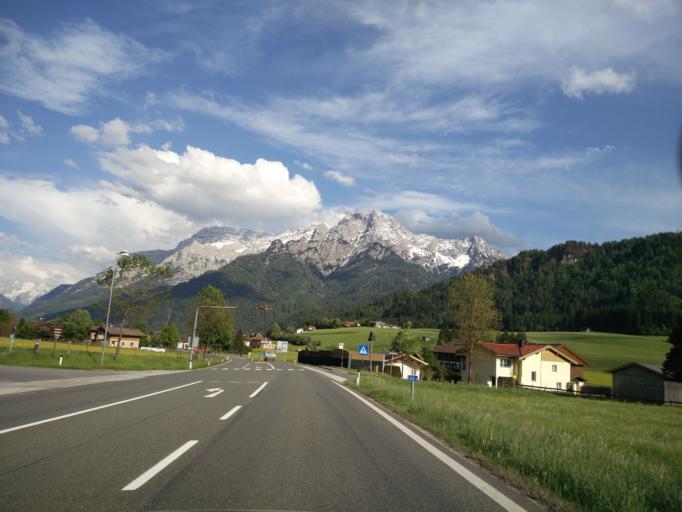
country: AT
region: Tyrol
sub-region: Politischer Bezirk Kitzbuhel
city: Waidring
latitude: 47.5907
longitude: 12.5509
